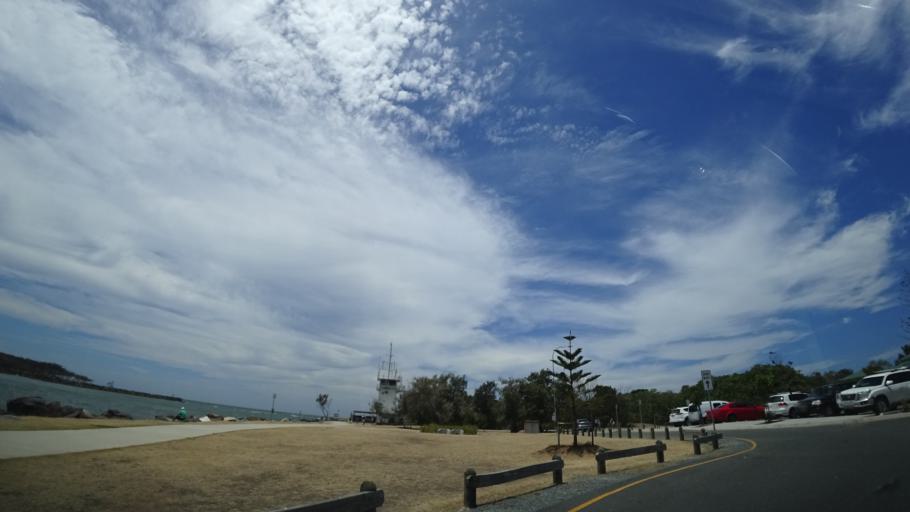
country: AU
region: Queensland
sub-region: Gold Coast
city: Southport
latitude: -27.9371
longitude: 153.4260
